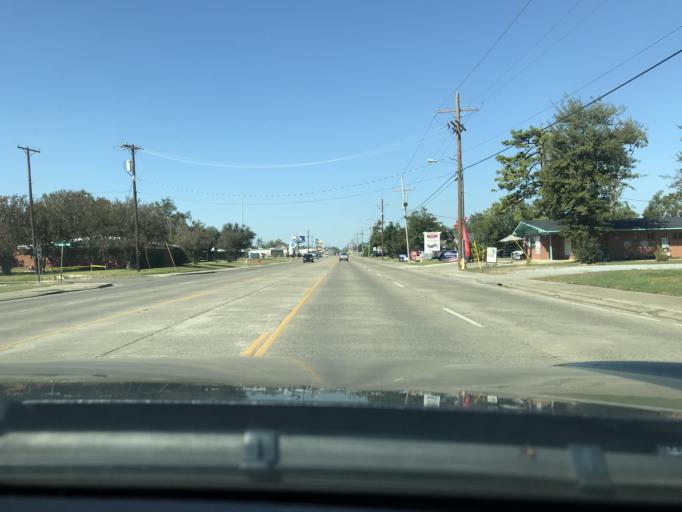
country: US
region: Louisiana
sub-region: Calcasieu Parish
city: Westlake
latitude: 30.2492
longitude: -93.2581
